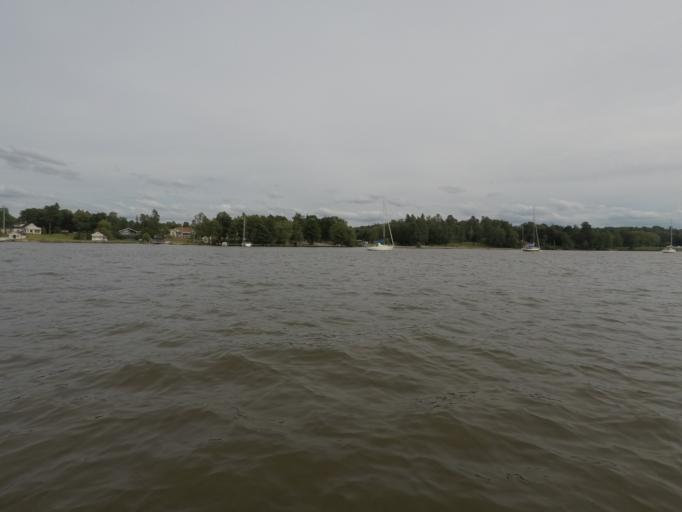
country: SE
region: Soedermanland
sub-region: Eskilstuna Kommun
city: Torshalla
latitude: 59.4541
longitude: 16.4320
